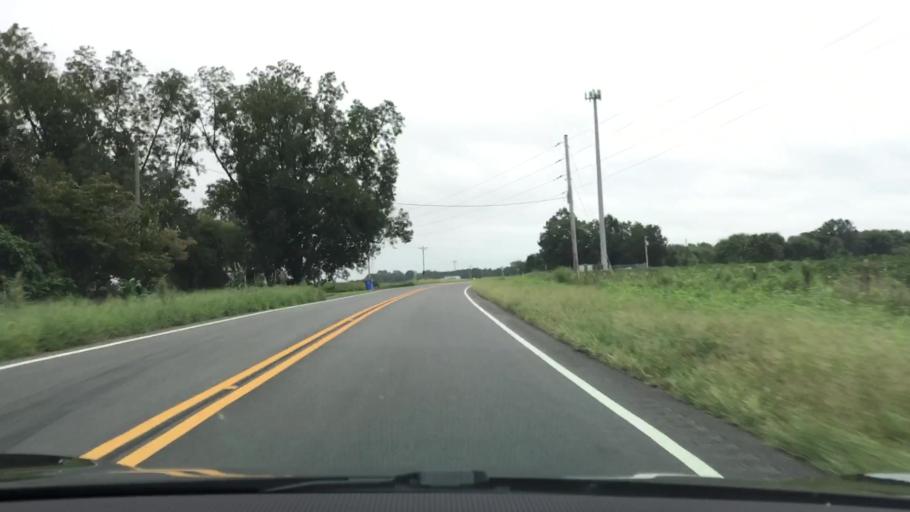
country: US
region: Alabama
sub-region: Covington County
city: Opp
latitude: 31.2667
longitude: -86.1621
